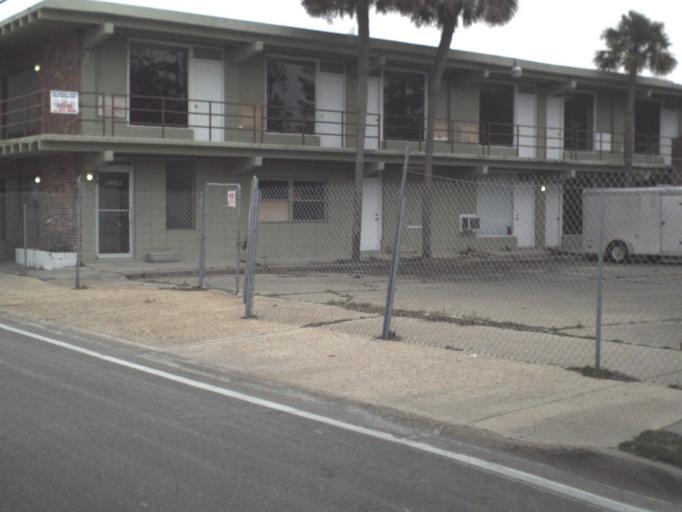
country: US
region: Florida
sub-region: Bay County
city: Pretty Bayou
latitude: 30.1706
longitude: -85.7015
